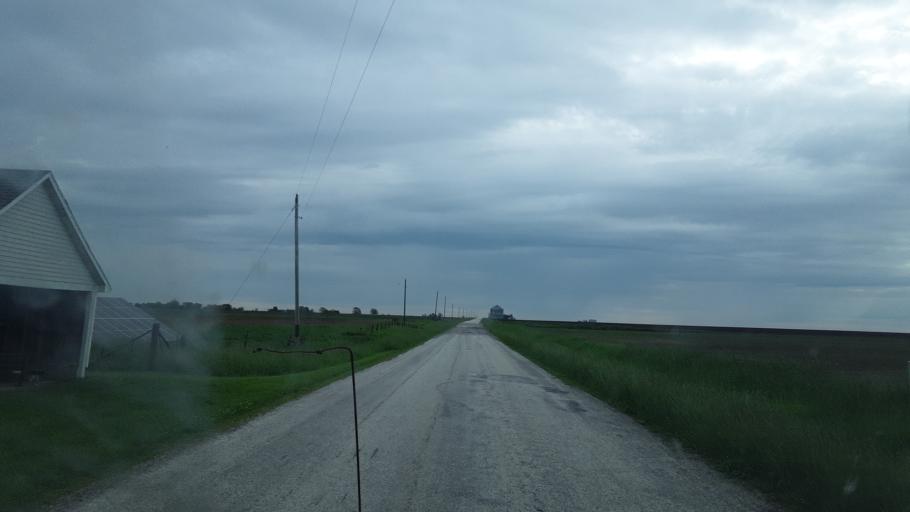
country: US
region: Illinois
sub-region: McDonough County
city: Macomb
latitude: 40.3821
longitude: -90.5832
